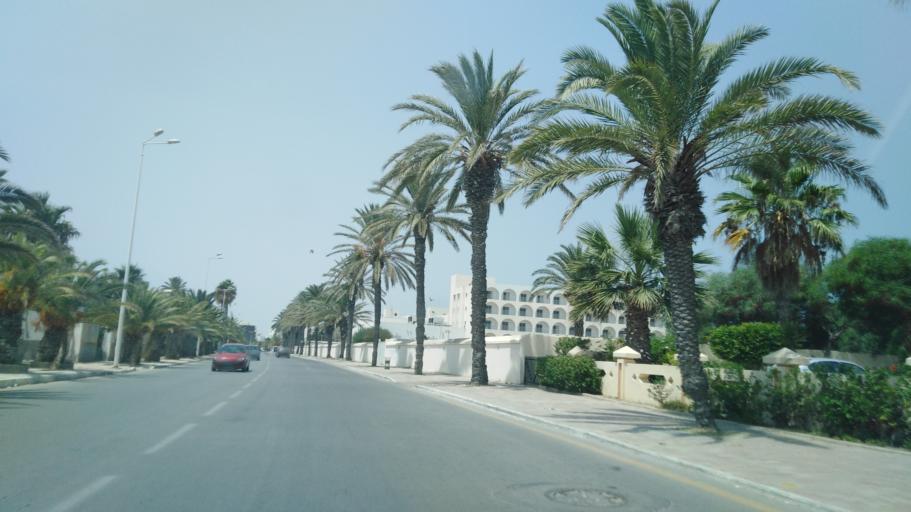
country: TN
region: Al Mahdiyah
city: Mahdia
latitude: 35.5154
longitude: 11.0462
